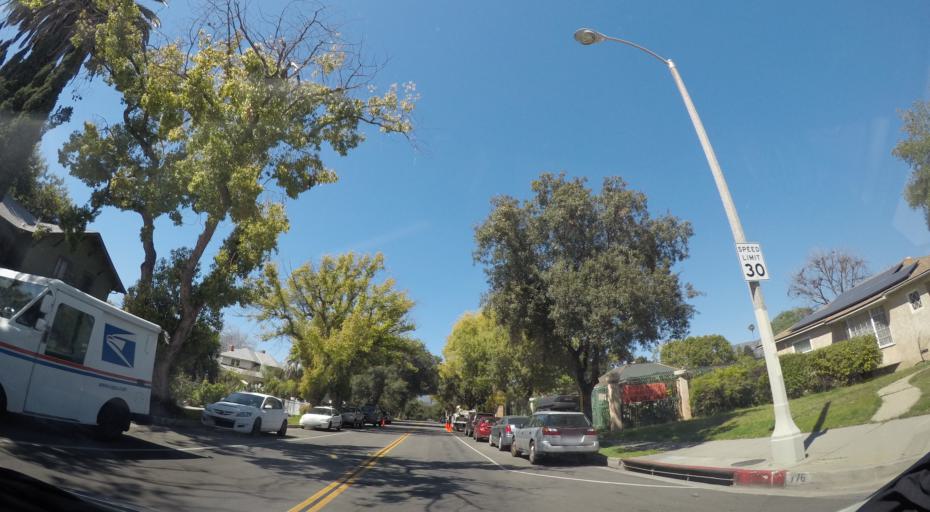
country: US
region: California
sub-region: Los Angeles County
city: Pasadena
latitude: 34.1578
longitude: -118.1564
